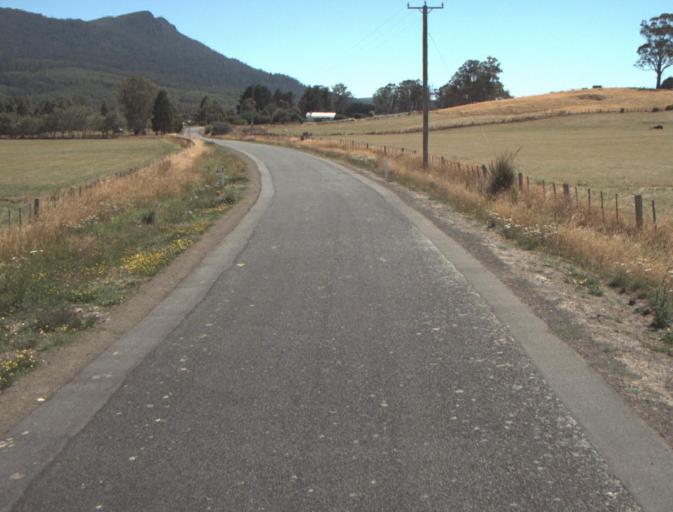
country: AU
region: Tasmania
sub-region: Launceston
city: Newstead
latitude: -41.3434
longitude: 147.3034
